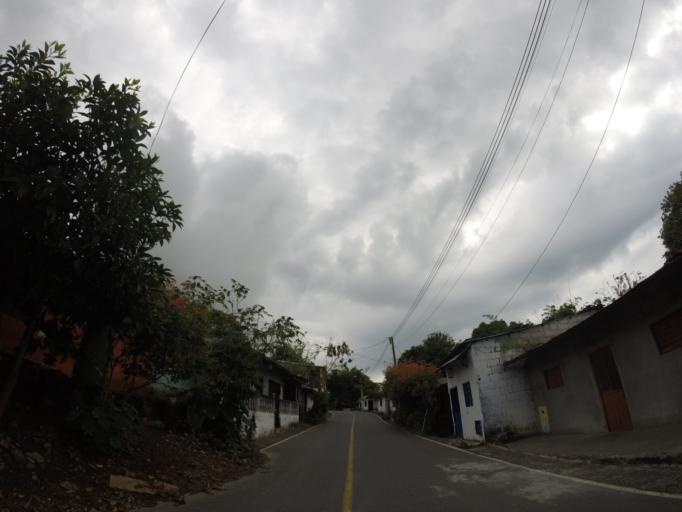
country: CO
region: Caldas
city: Victoria
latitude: 5.3216
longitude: -74.9128
